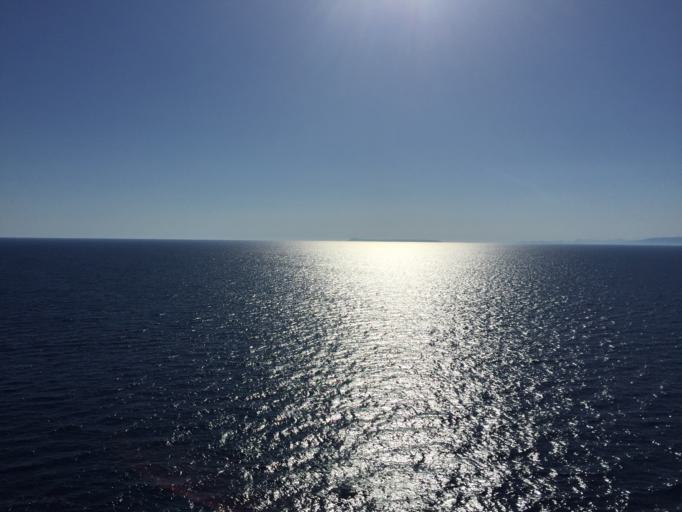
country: FR
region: Provence-Alpes-Cote d'Azur
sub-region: Departement du Var
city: Ramatuelle
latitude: 43.0674
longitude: 6.8458
